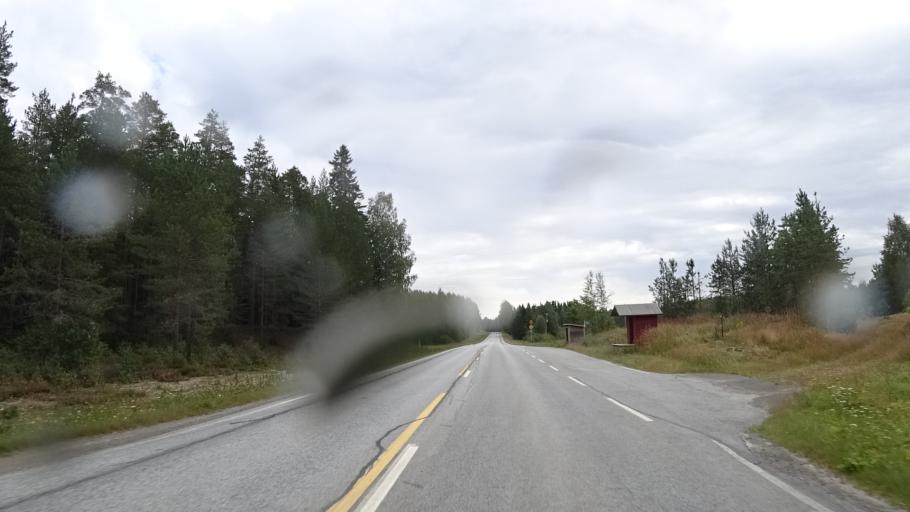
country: FI
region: North Karelia
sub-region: Keski-Karjala
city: Kesaelahti
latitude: 62.1103
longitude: 29.7395
